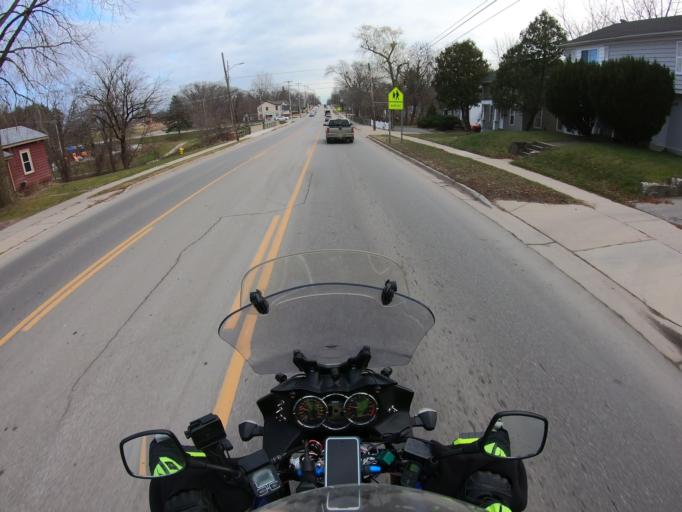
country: US
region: Michigan
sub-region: Genesee County
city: Clio
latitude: 43.1777
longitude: -83.7330
